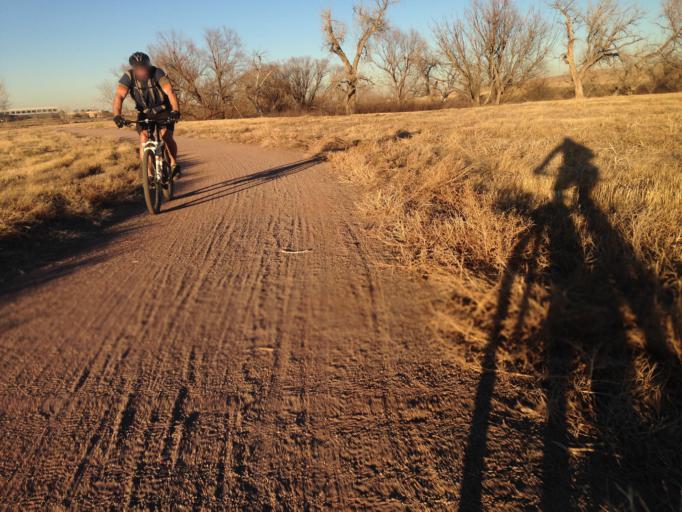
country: US
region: Colorado
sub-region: Boulder County
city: Lafayette
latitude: 39.9613
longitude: -105.0864
